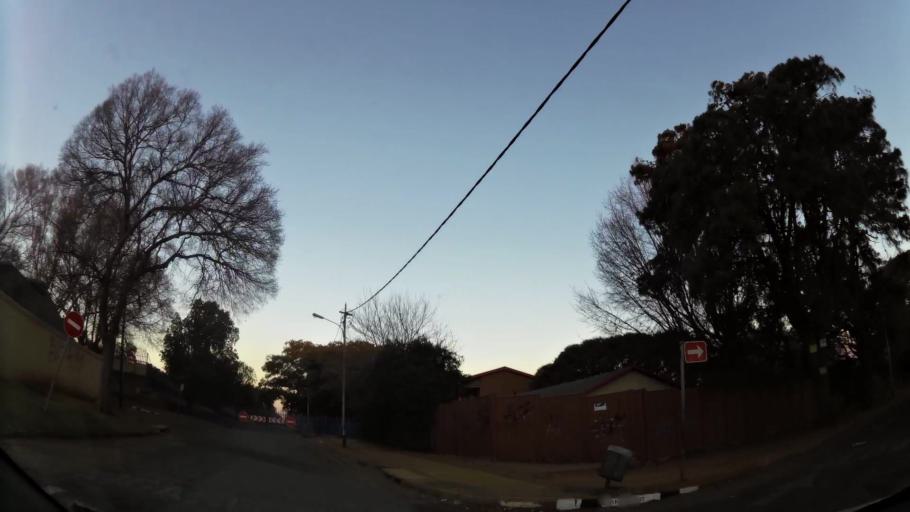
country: ZA
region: Gauteng
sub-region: City of Johannesburg Metropolitan Municipality
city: Roodepoort
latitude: -26.1752
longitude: 27.9160
